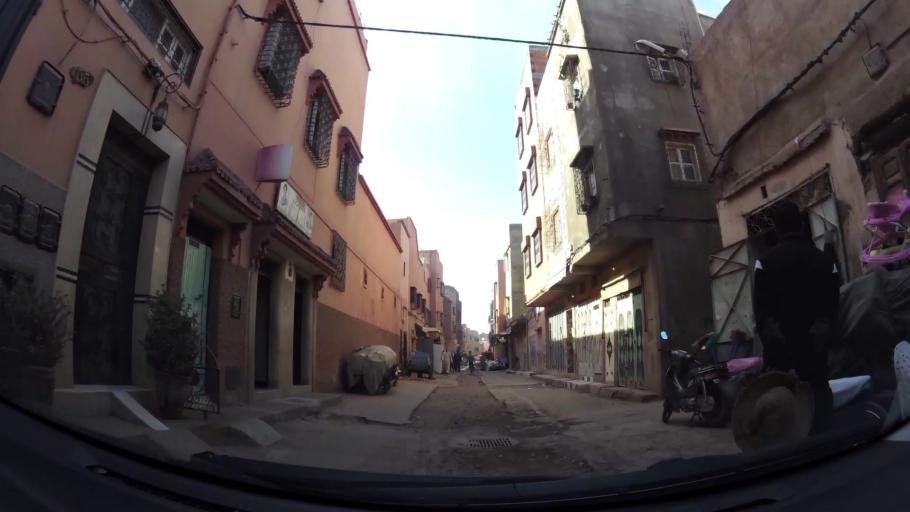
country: MA
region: Marrakech-Tensift-Al Haouz
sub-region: Marrakech
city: Marrakesh
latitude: 31.6114
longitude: -7.9645
